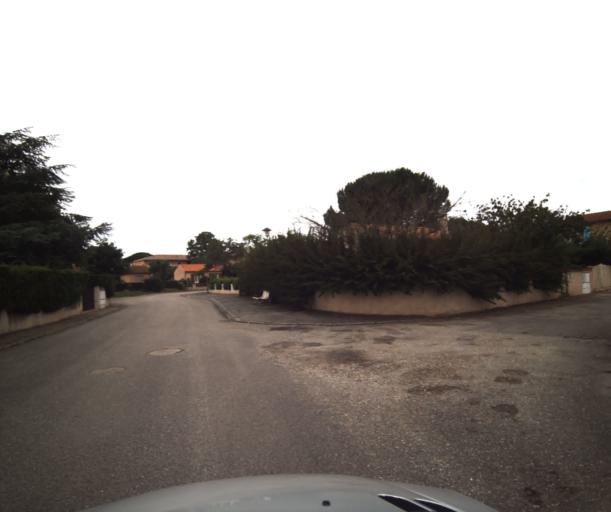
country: FR
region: Midi-Pyrenees
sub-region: Departement de la Haute-Garonne
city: Labarthe-sur-Leze
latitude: 43.4516
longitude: 1.4036
